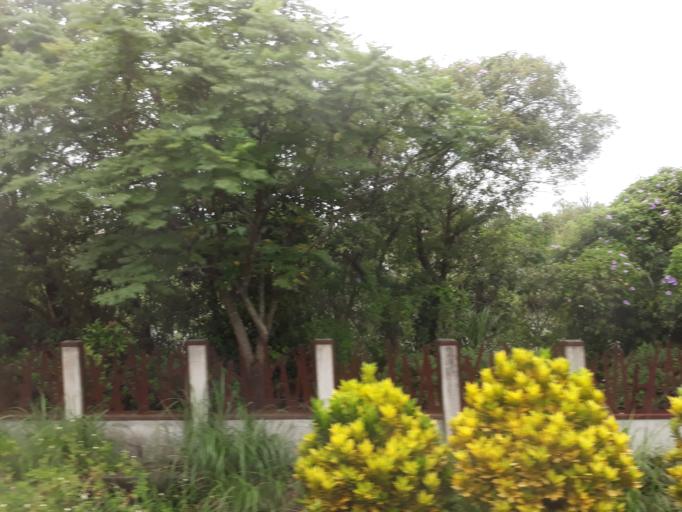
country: TW
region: Taiwan
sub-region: Yilan
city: Yilan
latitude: 24.6824
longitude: 121.7747
